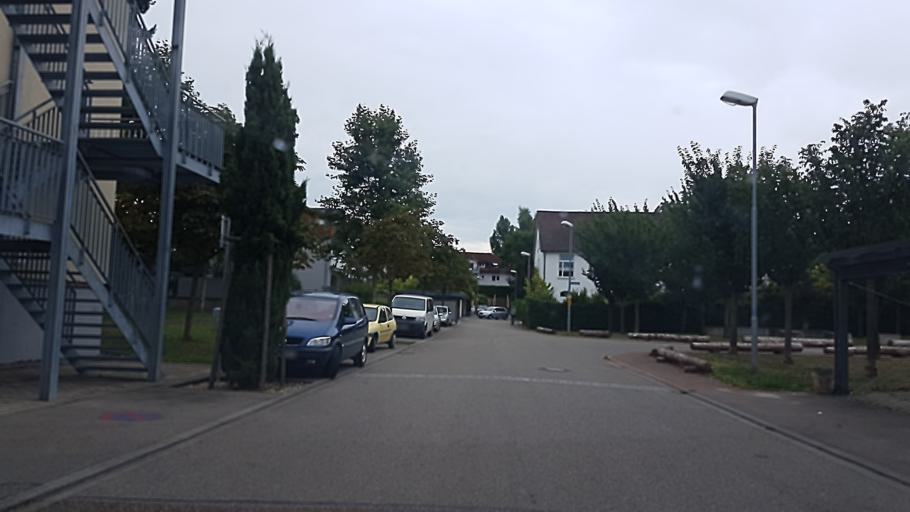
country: DE
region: Baden-Wuerttemberg
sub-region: Freiburg Region
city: Emmendingen
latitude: 48.1140
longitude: 7.8567
